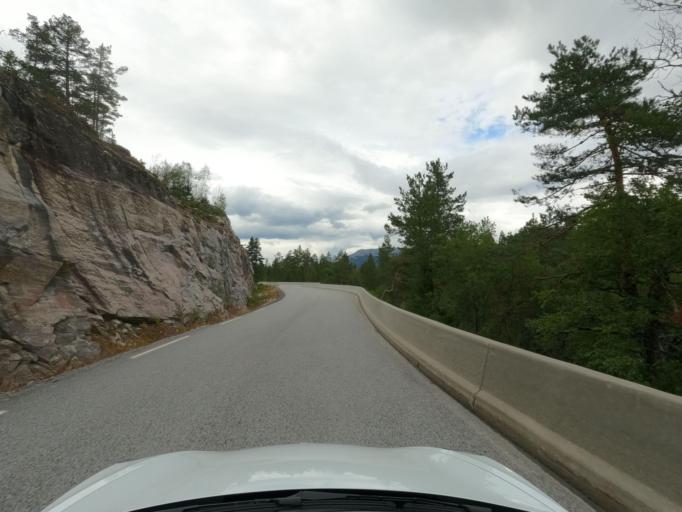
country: NO
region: Telemark
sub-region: Notodden
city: Notodden
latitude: 59.7059
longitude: 9.1510
